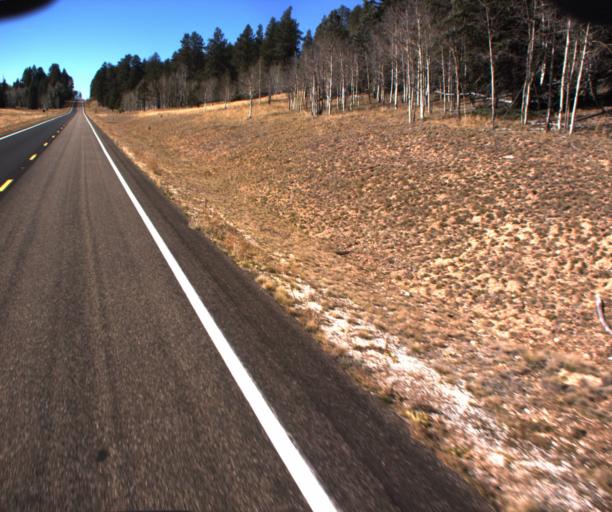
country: US
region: Arizona
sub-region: Coconino County
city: Grand Canyon
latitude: 36.5423
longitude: -112.1630
